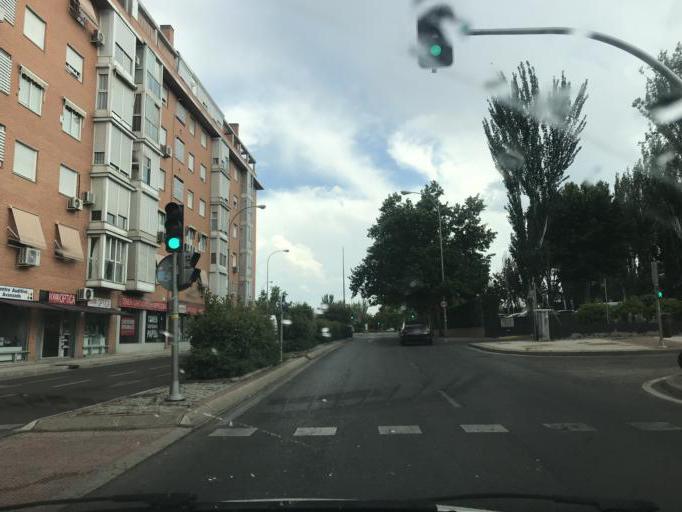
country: ES
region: Madrid
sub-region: Provincia de Madrid
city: Barajas de Madrid
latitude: 40.4704
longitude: -3.5815
